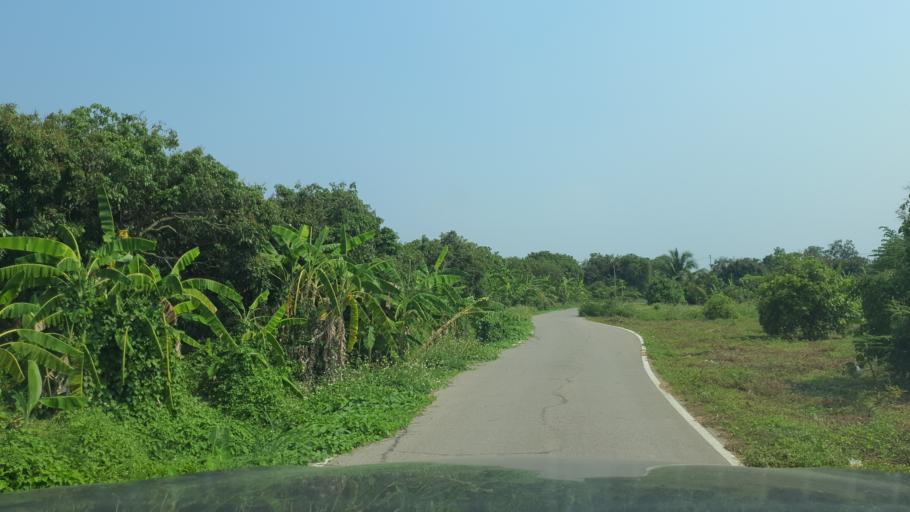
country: TH
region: Lamphun
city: Lamphun
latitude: 18.6475
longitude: 98.9871
